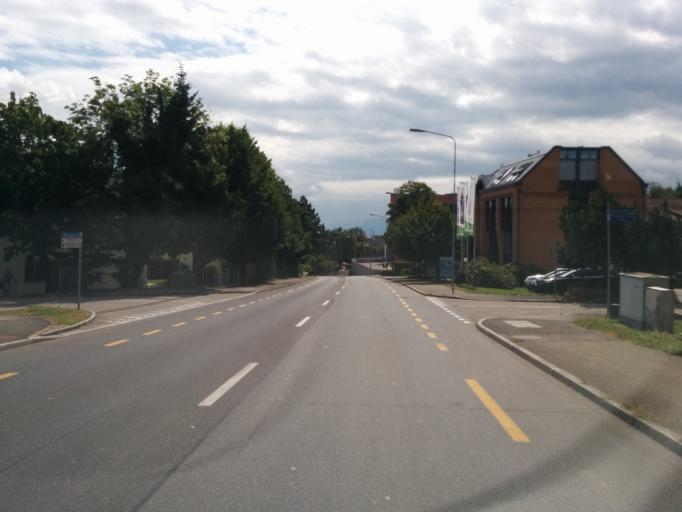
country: CH
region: Zurich
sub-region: Bezirk Horgen
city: Thalwil / Sued
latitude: 47.2860
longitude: 8.5681
